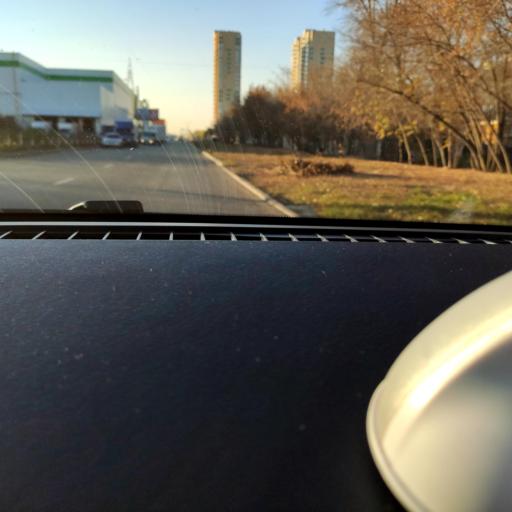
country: RU
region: Samara
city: Samara
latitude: 53.2091
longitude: 50.1938
